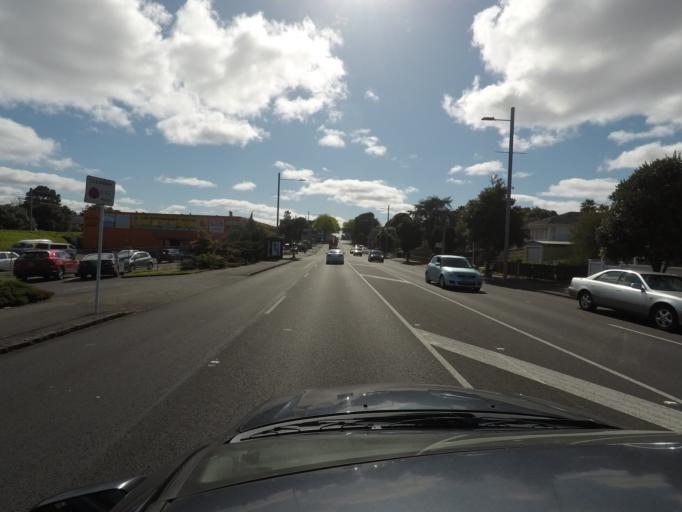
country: NZ
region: Auckland
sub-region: Auckland
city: Rosebank
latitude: -36.8871
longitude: 174.7124
